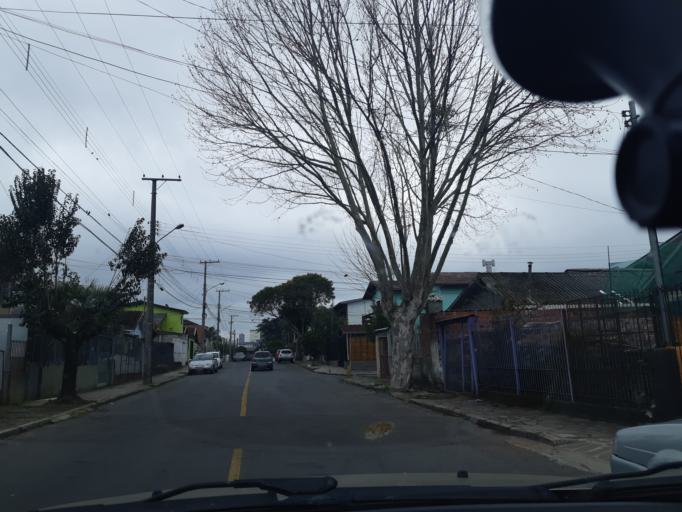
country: BR
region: Rio Grande do Sul
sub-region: Caxias Do Sul
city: Caxias do Sul
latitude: -29.1537
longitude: -51.2090
